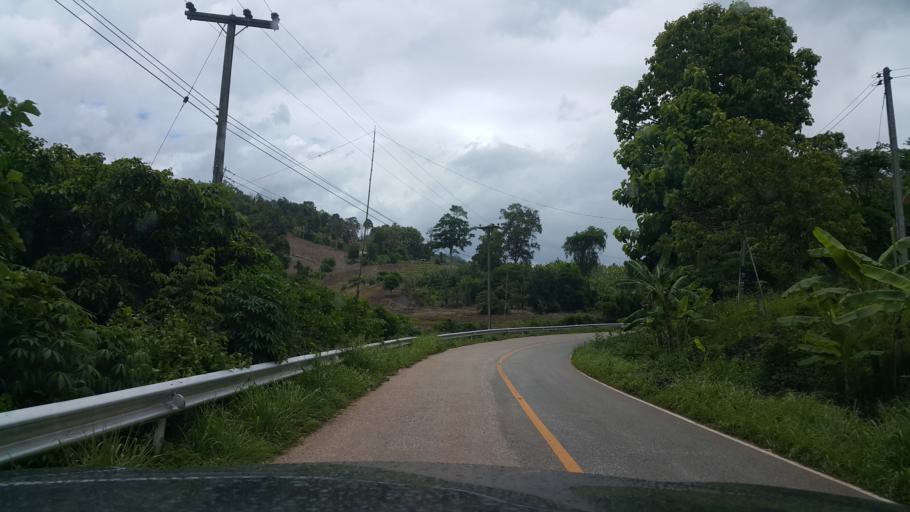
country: TH
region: Loei
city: Na Haeo
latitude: 17.5416
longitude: 100.8365
